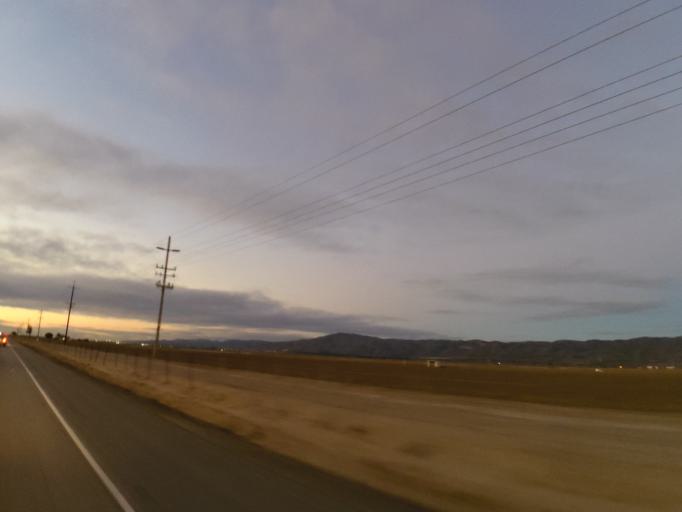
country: US
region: California
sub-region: Monterey County
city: Soledad
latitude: 36.3746
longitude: -121.2894
